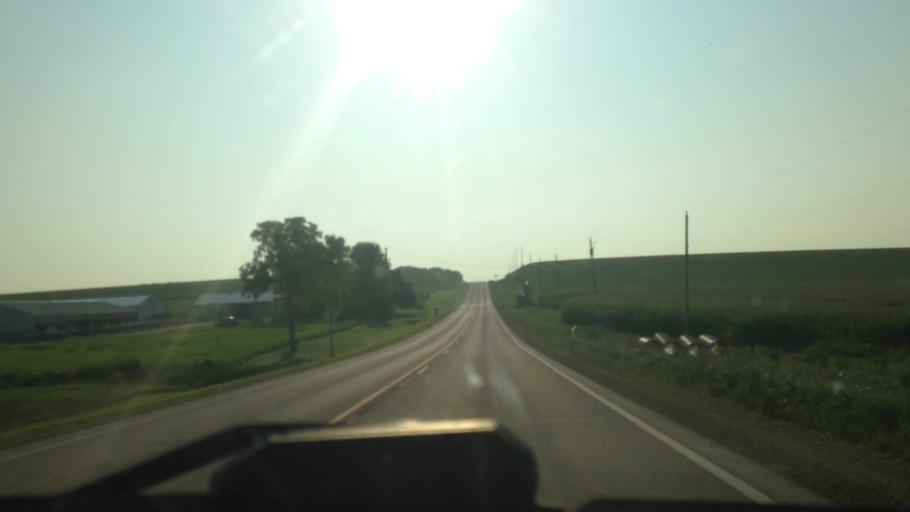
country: US
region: Wisconsin
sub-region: Dodge County
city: Theresa
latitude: 43.5364
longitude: -88.4630
